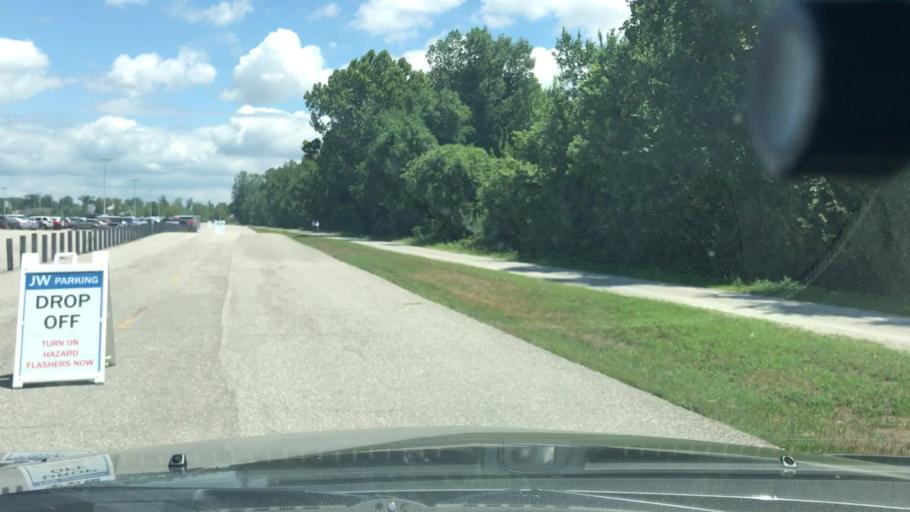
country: US
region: Missouri
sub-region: Saint Charles County
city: Saint Charles
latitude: 38.7454
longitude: -90.5101
